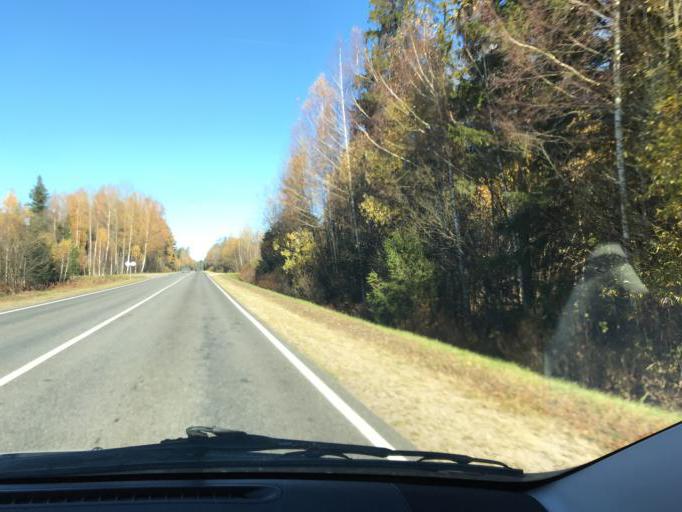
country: BY
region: Vitebsk
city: Lyepyel'
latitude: 54.9838
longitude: 28.7426
